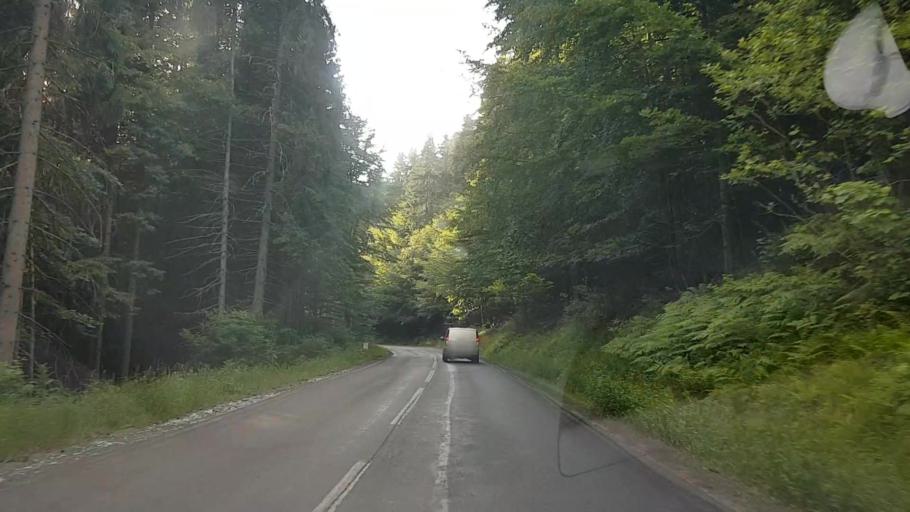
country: RO
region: Harghita
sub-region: Comuna Varsag
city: Varsag
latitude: 46.6647
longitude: 25.3140
